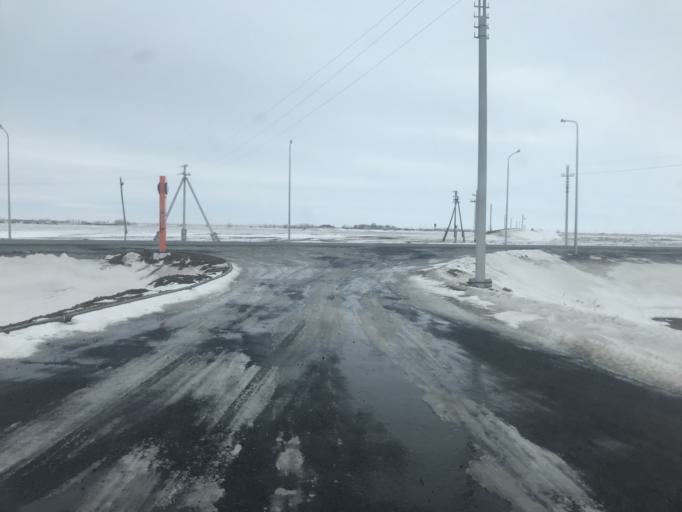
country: KZ
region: Batys Qazaqstan
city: Oral
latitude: 51.4042
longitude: 51.2972
